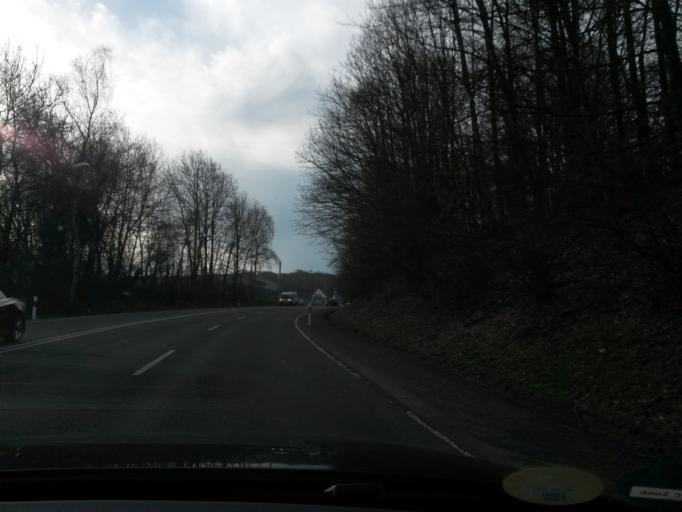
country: DE
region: North Rhine-Westphalia
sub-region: Regierungsbezirk Arnsberg
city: Luedenscheid
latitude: 51.2379
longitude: 7.6083
